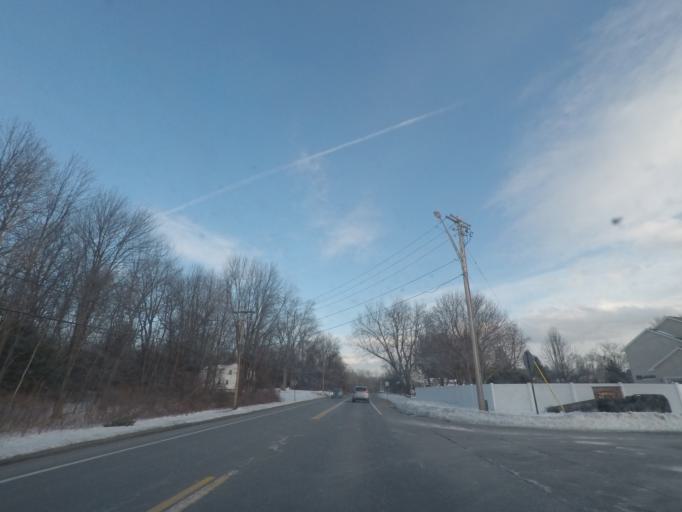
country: US
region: New York
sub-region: Saratoga County
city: Country Knolls
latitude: 42.8400
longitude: -73.7871
